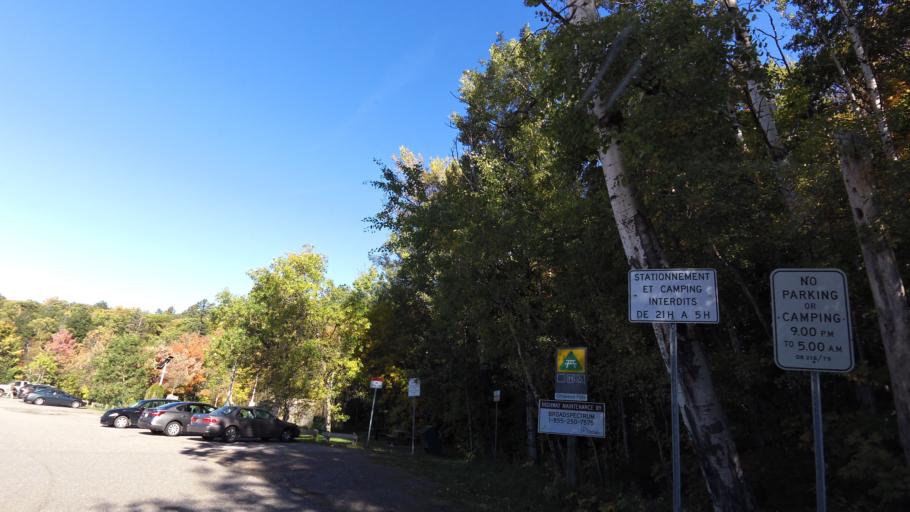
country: CA
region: Ontario
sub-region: Algoma
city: Sault Ste. Marie
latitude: 46.9280
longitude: -84.4250
